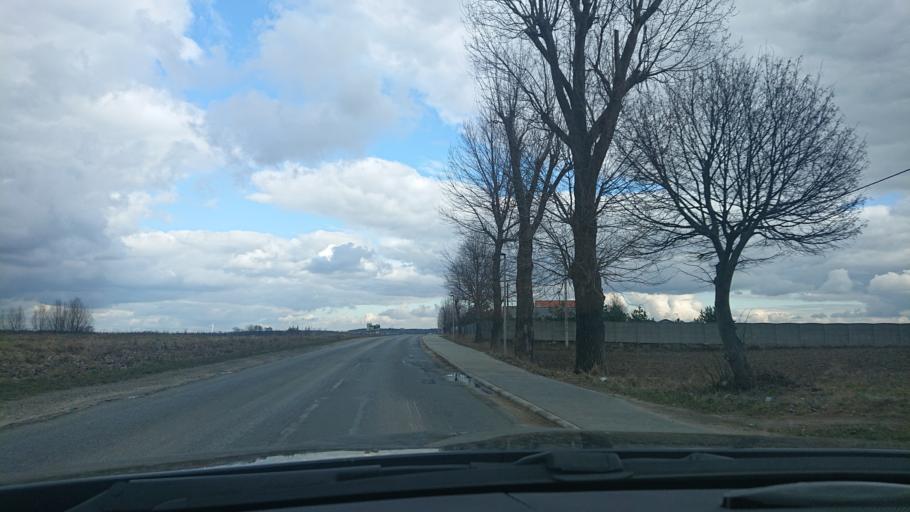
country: PL
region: Greater Poland Voivodeship
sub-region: Powiat gnieznienski
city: Niechanowo
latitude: 52.5481
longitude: 17.6724
